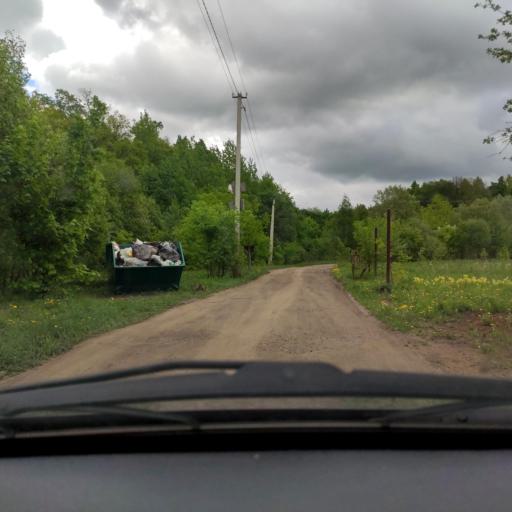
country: RU
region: Bashkortostan
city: Kabakovo
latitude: 54.7066
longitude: 56.1608
